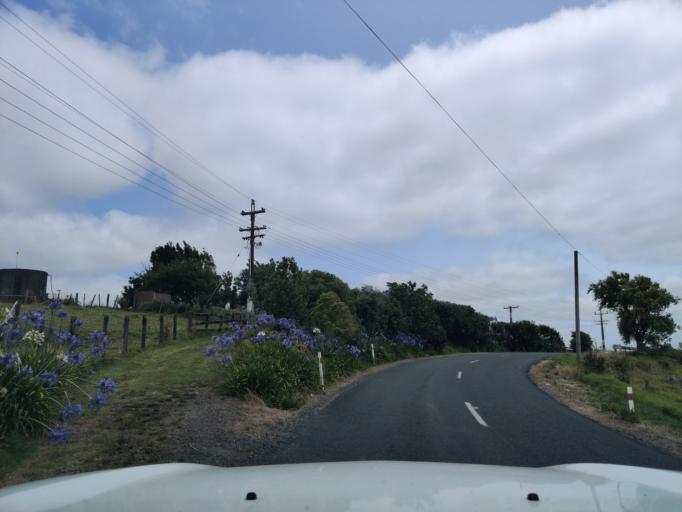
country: NZ
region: Waikato
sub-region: Waikato District
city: Te Kauwhata
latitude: -37.5218
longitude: 175.1769
